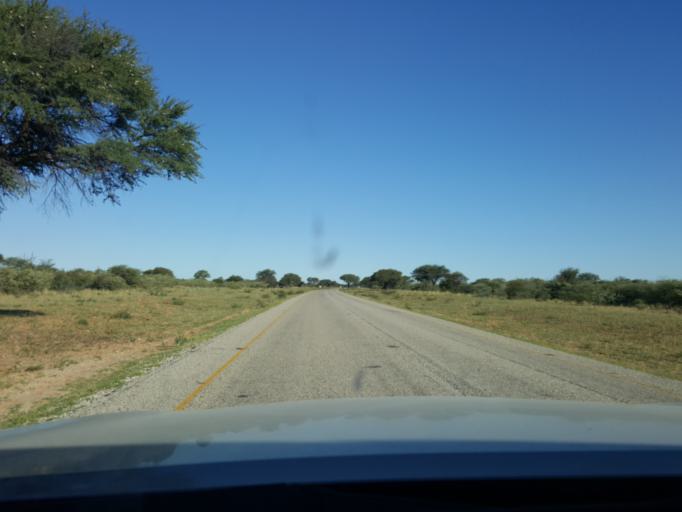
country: BW
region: Kgalagadi
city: Kang
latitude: -24.0241
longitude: 23.0384
